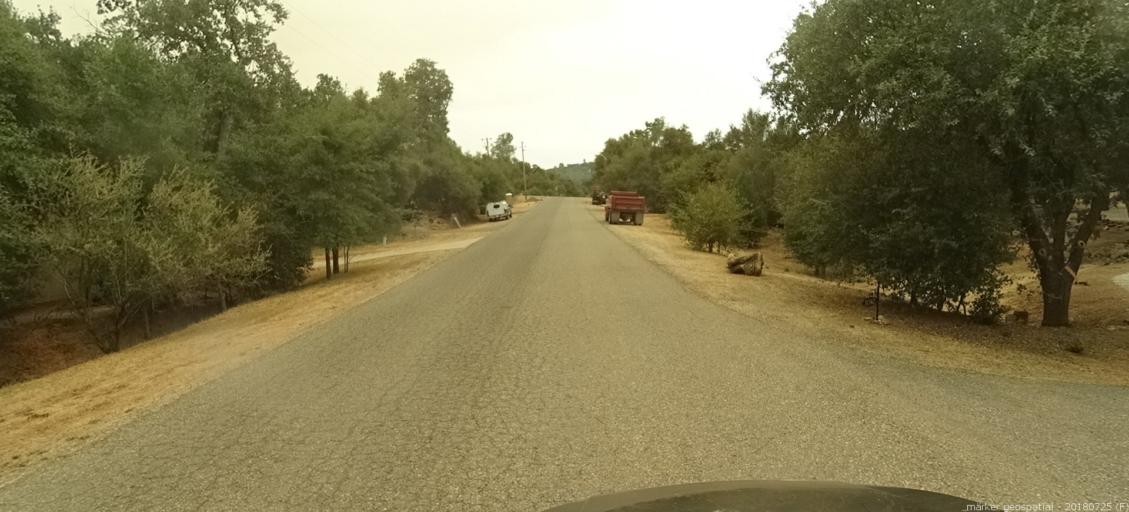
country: US
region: California
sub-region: Madera County
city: Coarsegold
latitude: 37.2049
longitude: -119.6766
